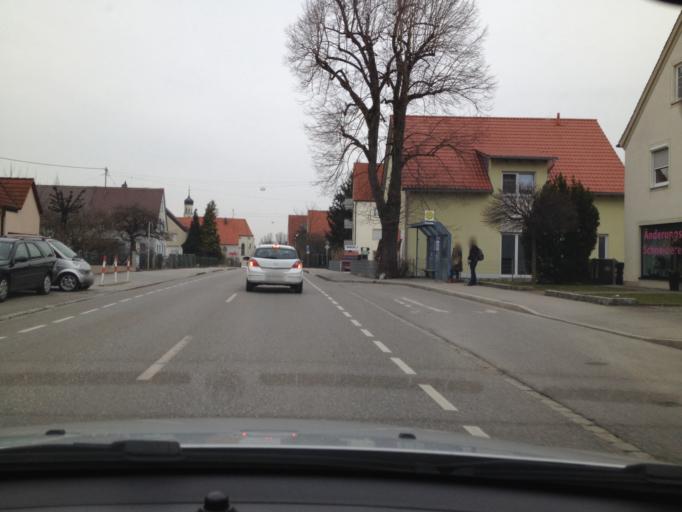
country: DE
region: Bavaria
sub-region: Swabia
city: Bobingen
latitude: 48.2752
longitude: 10.8386
